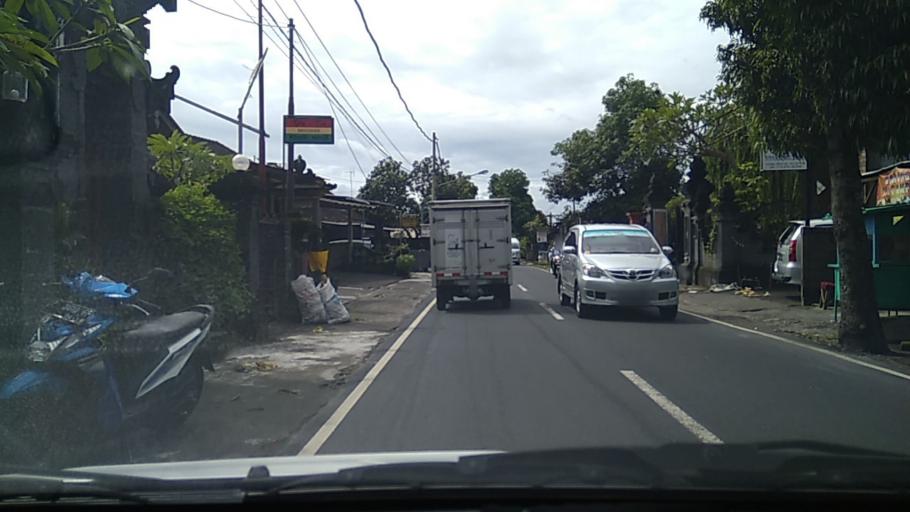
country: ID
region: Bali
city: Banjar Sedang
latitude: -8.5719
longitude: 115.2566
